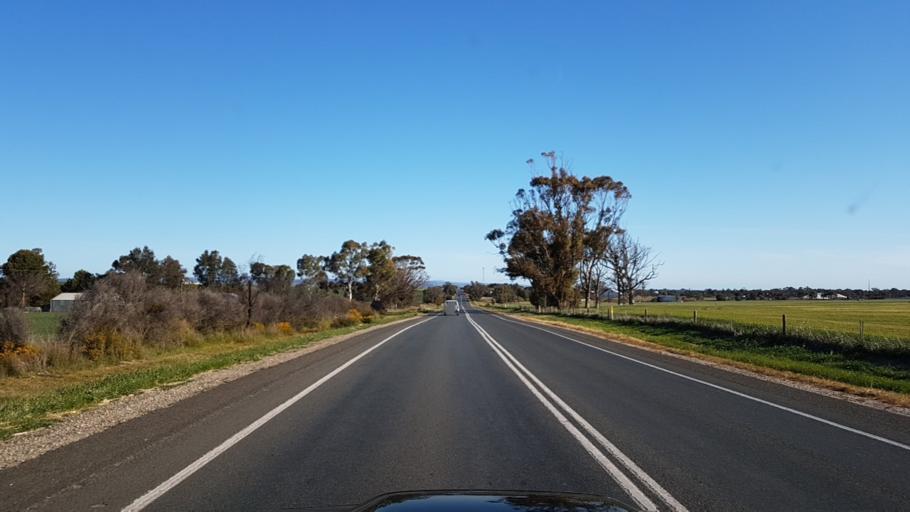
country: AU
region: South Australia
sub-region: Light
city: Roseworthy
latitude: -34.5140
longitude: 138.7531
